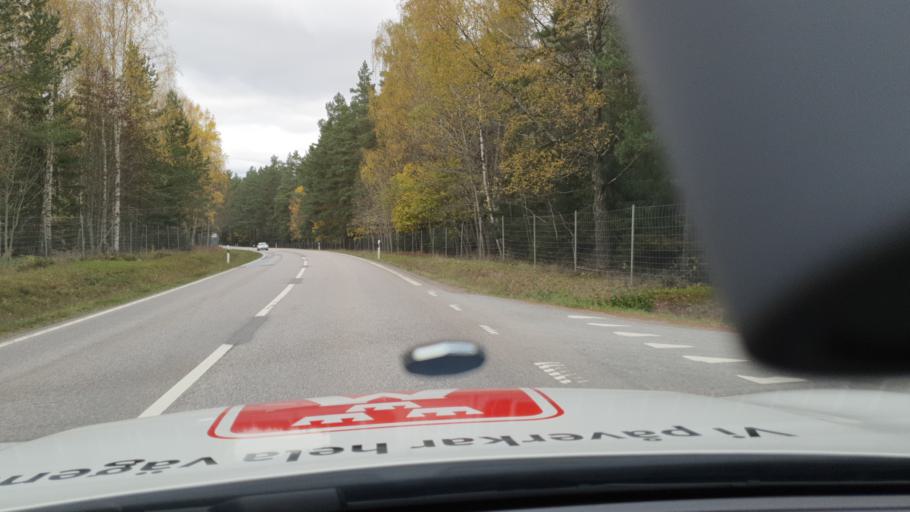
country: SE
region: OErebro
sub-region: Hallsbergs Kommun
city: Palsboda
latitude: 59.0073
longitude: 15.4020
